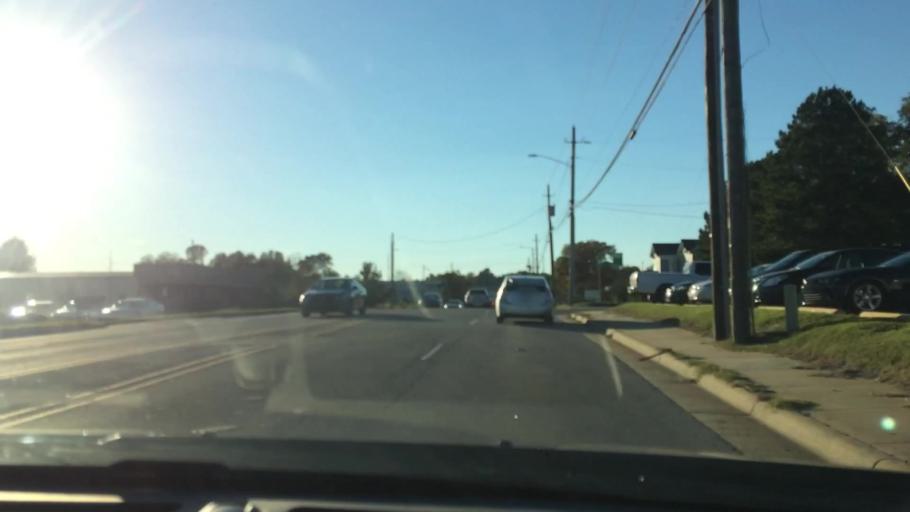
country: US
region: North Carolina
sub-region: Pitt County
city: Greenville
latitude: 35.6021
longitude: -77.3771
